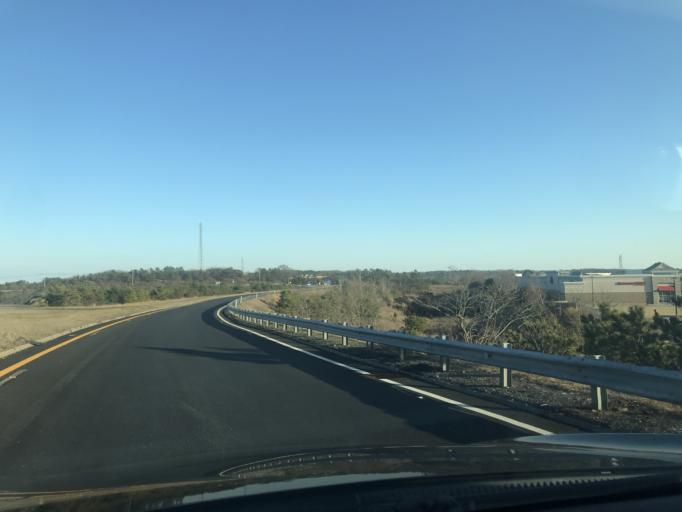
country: US
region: Massachusetts
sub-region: Plymouth County
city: North Plymouth
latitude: 41.9579
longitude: -70.7164
